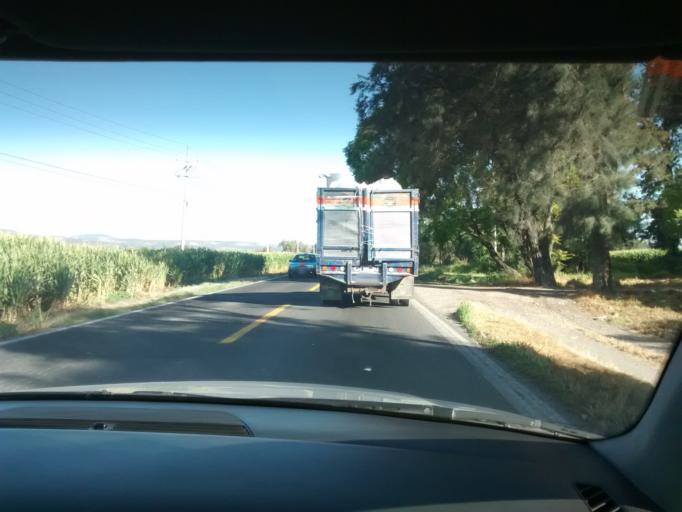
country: MX
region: Puebla
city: San Bartolo Teontepec
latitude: 18.5345
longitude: -97.5275
